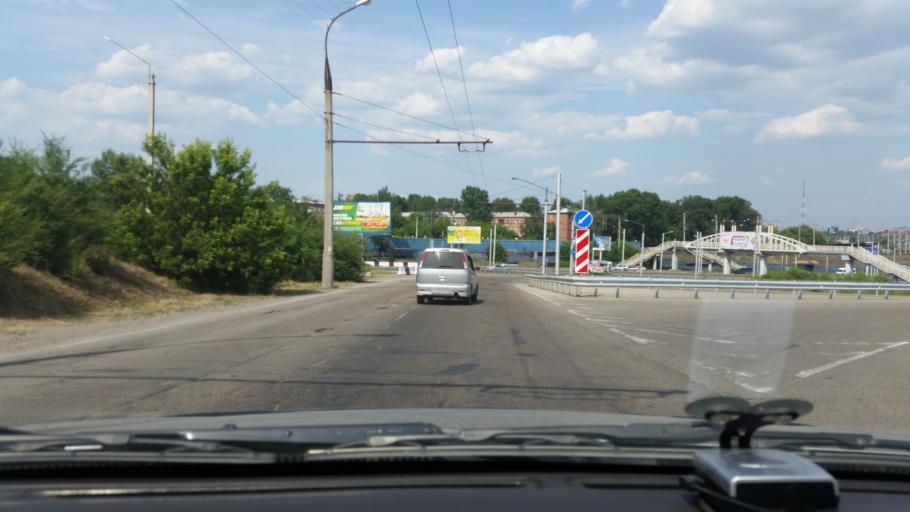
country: RU
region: Irkutsk
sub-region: Irkutskiy Rayon
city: Irkutsk
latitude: 52.2533
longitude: 104.2647
